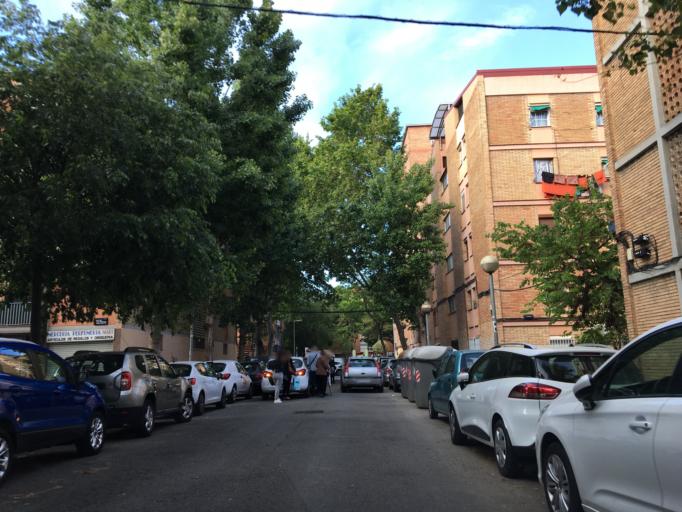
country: ES
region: Catalonia
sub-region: Provincia de Barcelona
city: Llefia
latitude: 41.4383
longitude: 2.2297
